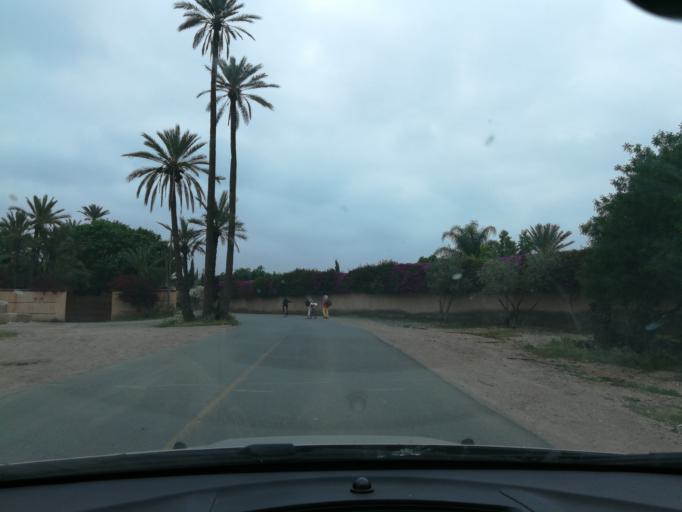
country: MA
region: Marrakech-Tensift-Al Haouz
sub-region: Marrakech
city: Marrakesh
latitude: 31.6740
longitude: -7.9852
